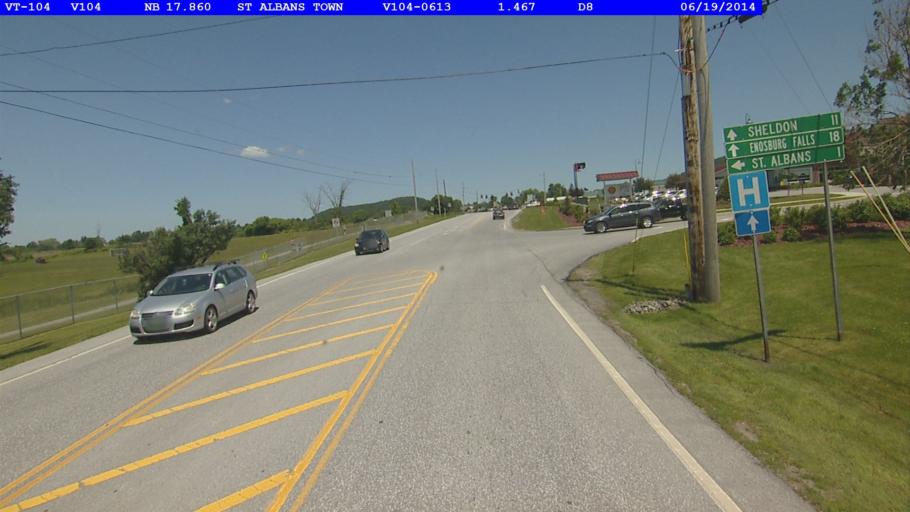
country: US
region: Vermont
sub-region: Franklin County
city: Saint Albans
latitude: 44.7944
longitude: -73.0740
